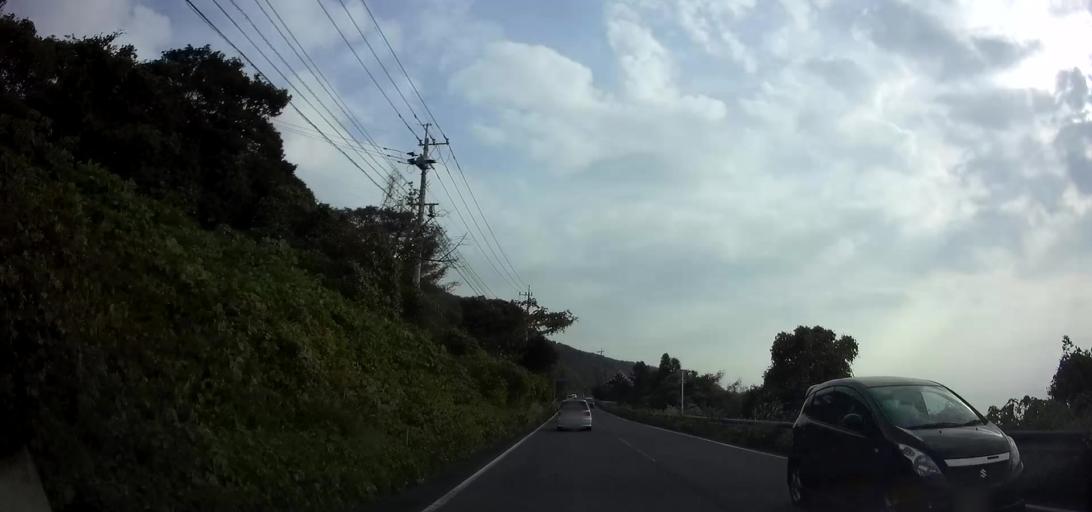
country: JP
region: Nagasaki
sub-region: Isahaya-shi
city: Isahaya
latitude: 32.7950
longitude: 130.0992
